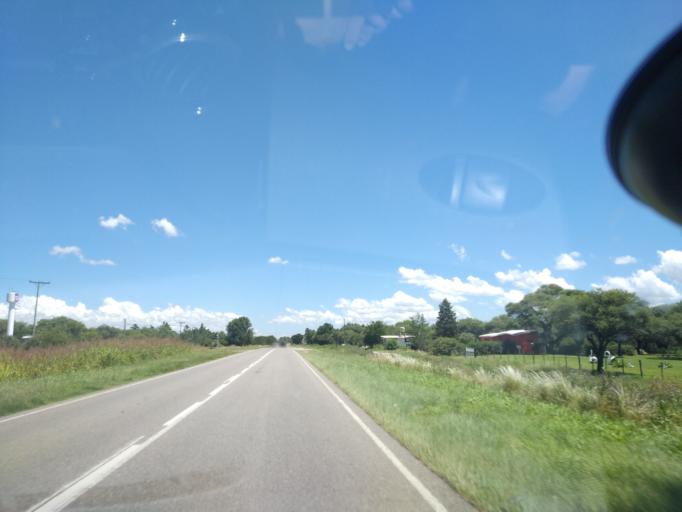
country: AR
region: Cordoba
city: Salsacate
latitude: -31.4881
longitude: -65.1080
